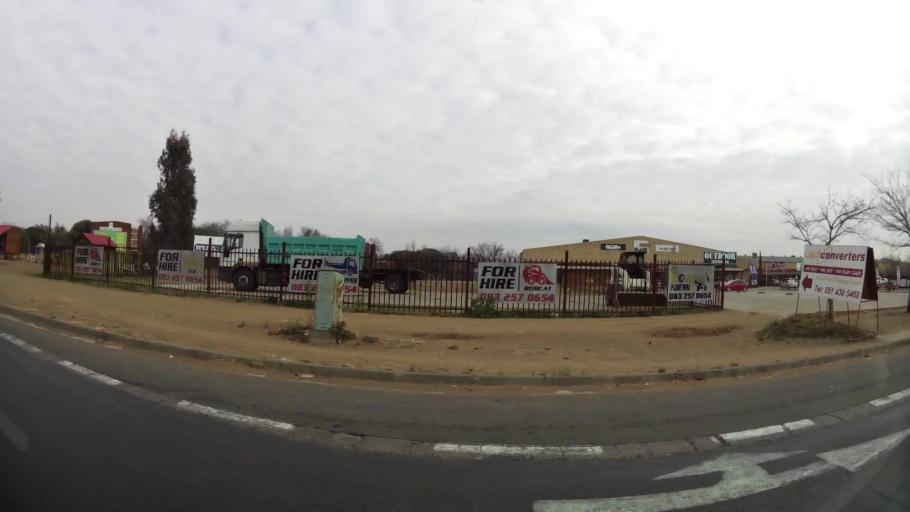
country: ZA
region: Orange Free State
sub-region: Mangaung Metropolitan Municipality
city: Bloemfontein
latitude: -29.1361
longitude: 26.2036
